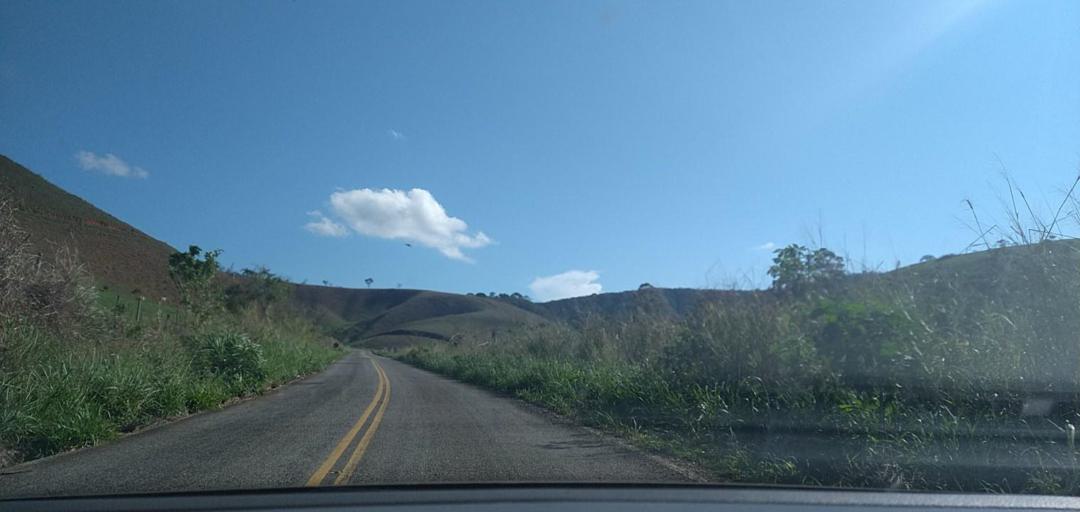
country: BR
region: Minas Gerais
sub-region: Alvinopolis
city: Alvinopolis
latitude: -20.1875
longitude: -42.9377
